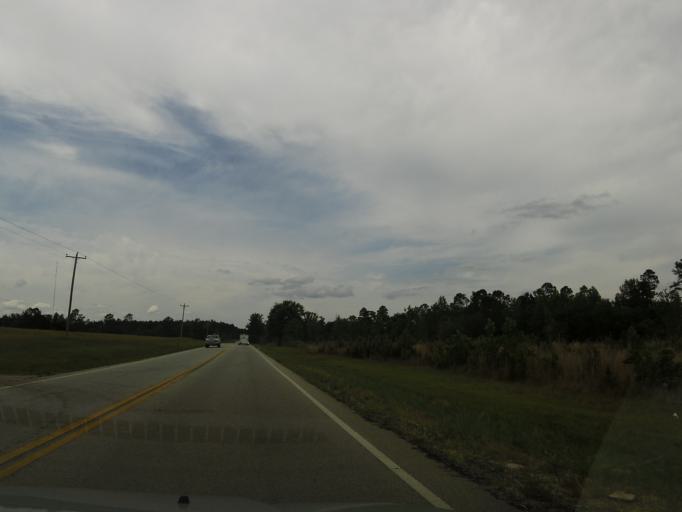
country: US
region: Georgia
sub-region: Emanuel County
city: Twin City
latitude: 32.4928
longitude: -82.2484
